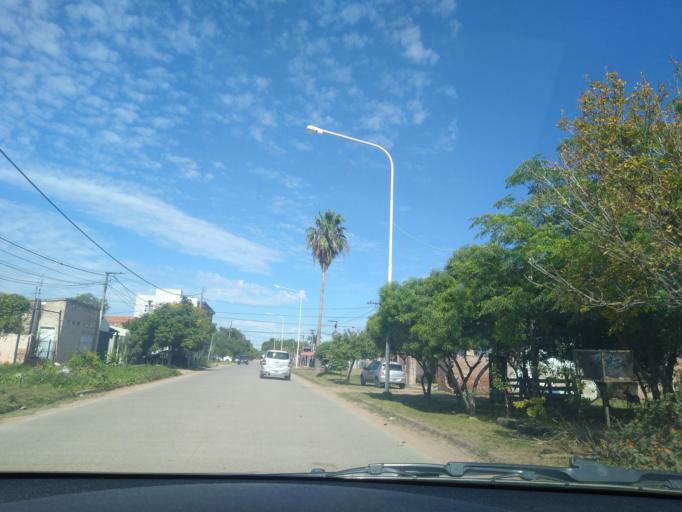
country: AR
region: Chaco
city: Presidencia Roque Saenz Pena
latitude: -26.7786
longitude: -60.4258
